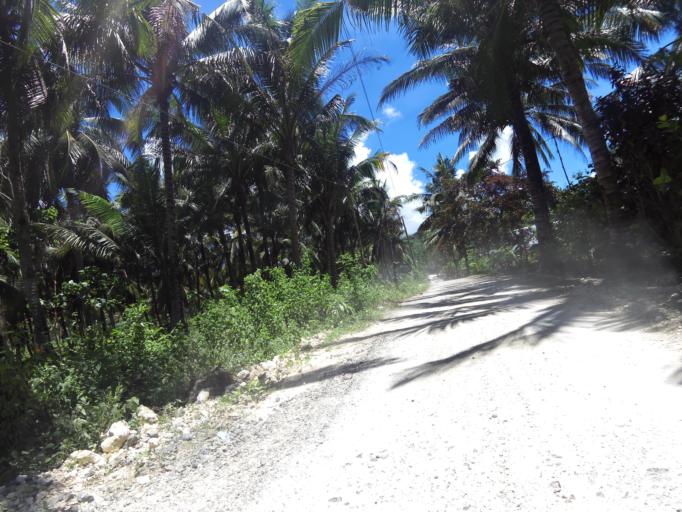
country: PH
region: Central Visayas
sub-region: Province of Bohol
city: Candabong
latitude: 9.7313
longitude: 124.5325
